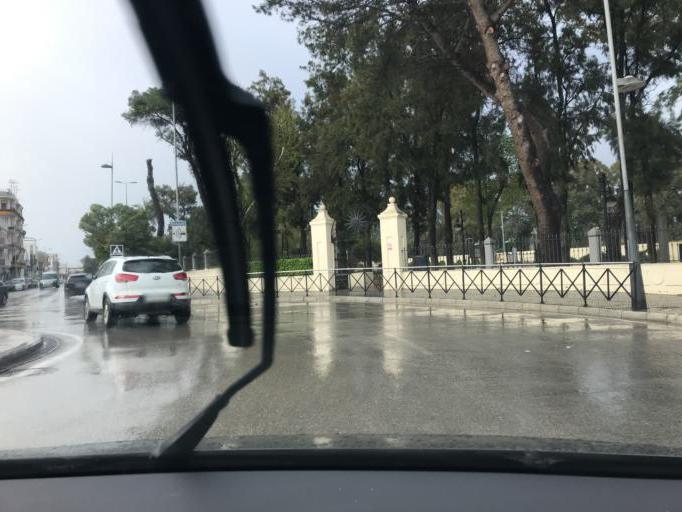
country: ES
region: Andalusia
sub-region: Provincia de Sevilla
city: Ecija
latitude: 37.5385
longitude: -5.0729
